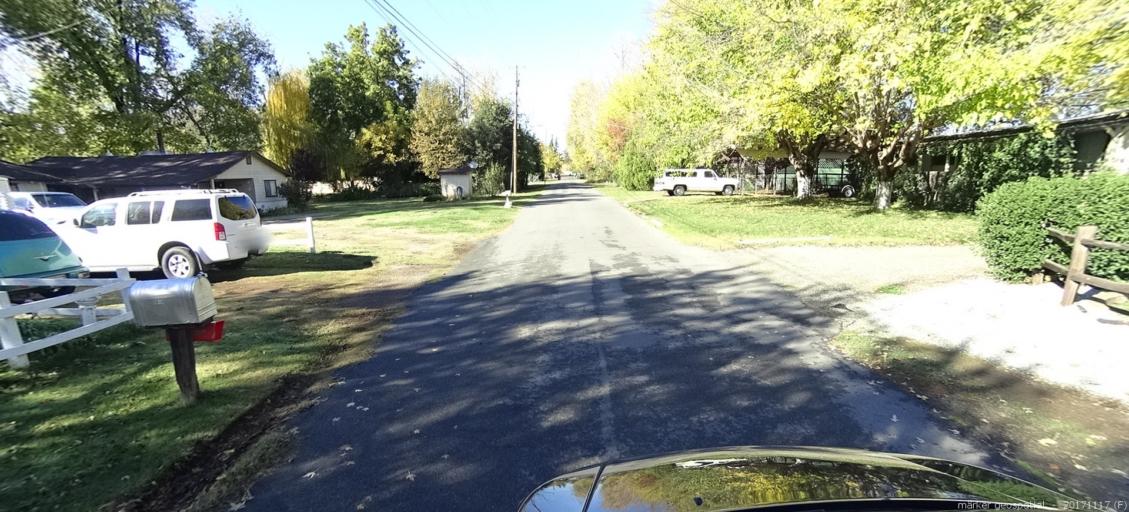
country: US
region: California
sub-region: Shasta County
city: Anderson
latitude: 40.4499
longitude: -122.2407
